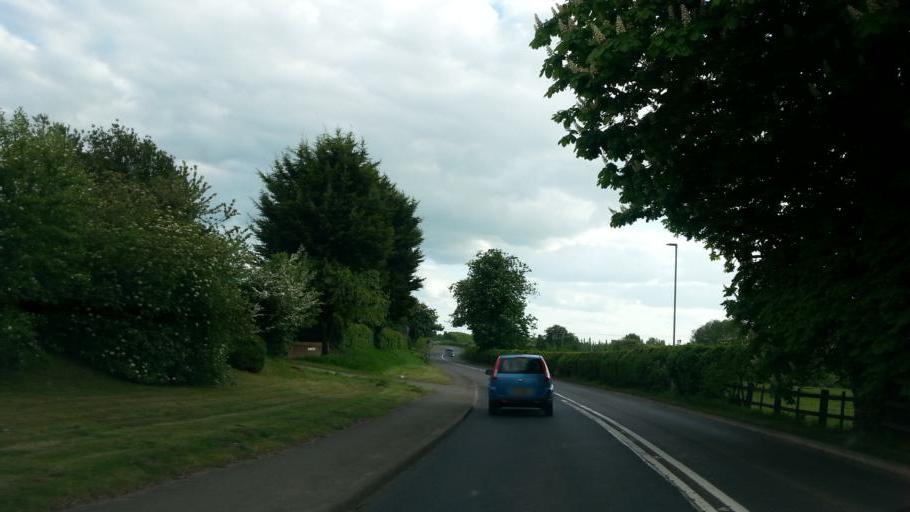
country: GB
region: England
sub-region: Nottinghamshire
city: South Collingham
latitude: 53.1144
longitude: -0.7740
